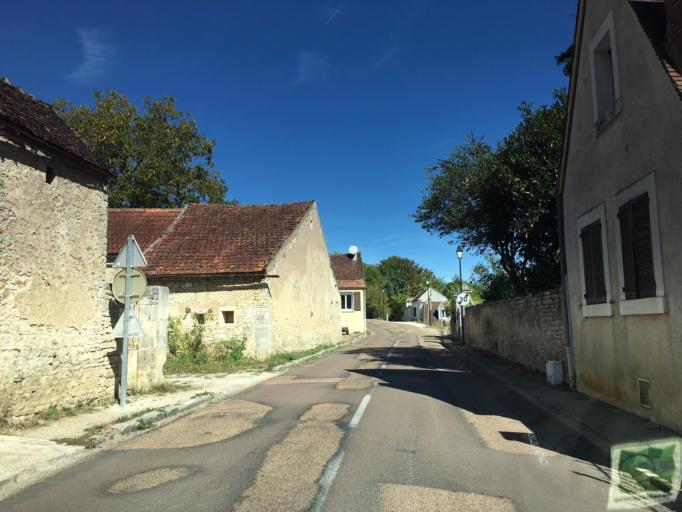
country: FR
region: Bourgogne
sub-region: Departement de l'Yonne
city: Vermenton
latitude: 47.6297
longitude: 3.6604
